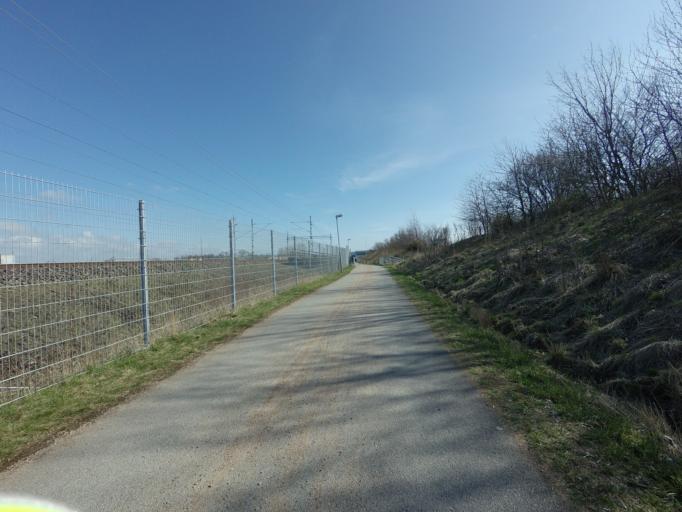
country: SE
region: Skane
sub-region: Landskrona
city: Landskrona
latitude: 55.8767
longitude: 12.8588
